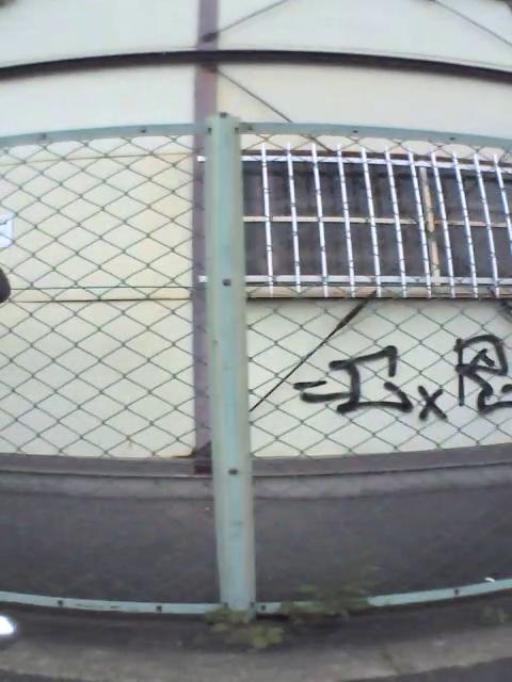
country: JP
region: Osaka
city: Hirakata
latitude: 34.8252
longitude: 135.6501
